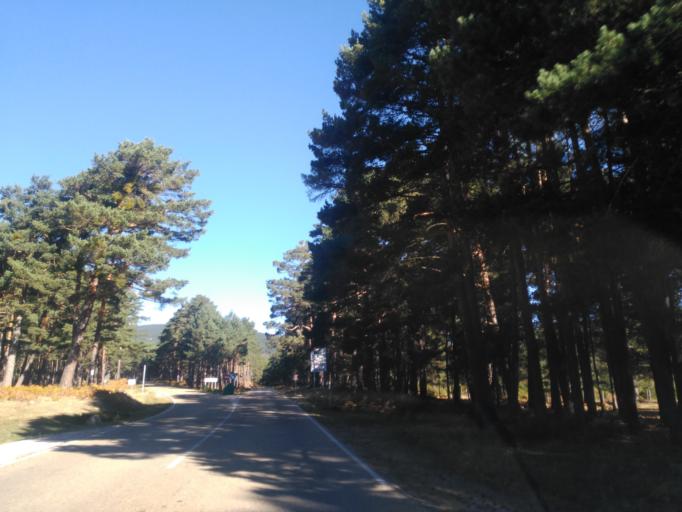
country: ES
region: Castille and Leon
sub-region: Provincia de Soria
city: Vinuesa
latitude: 41.9970
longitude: -2.7997
